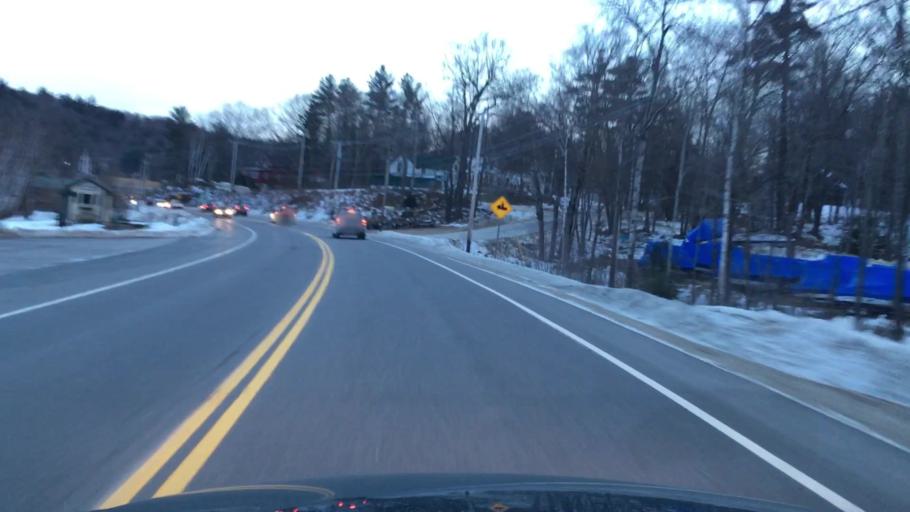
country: US
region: New Hampshire
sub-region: Merrimack County
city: Newbury
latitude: 43.3229
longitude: -72.0410
